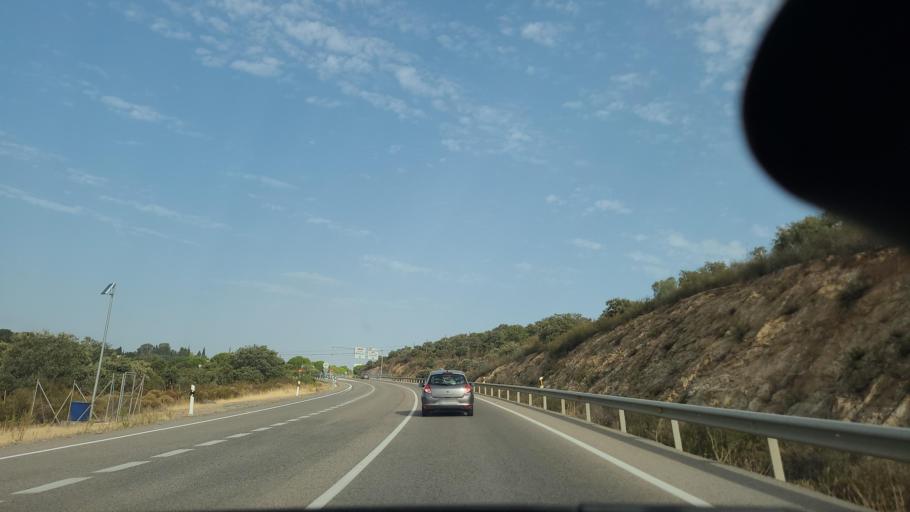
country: ES
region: Andalusia
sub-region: Province of Cordoba
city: Espiel
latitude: 38.1695
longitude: -4.9937
